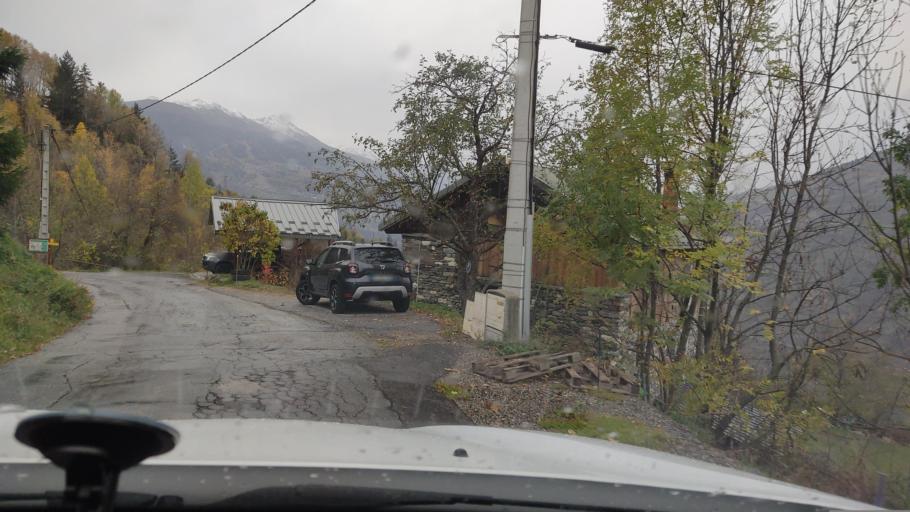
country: FR
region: Rhone-Alpes
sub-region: Departement de la Savoie
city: Bourg-Saint-Maurice
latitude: 45.5994
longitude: 6.7765
